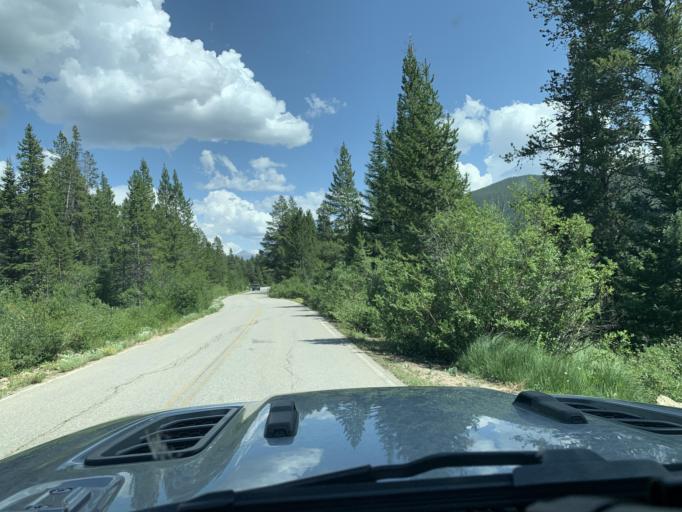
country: US
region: Colorado
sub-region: Lake County
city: Leadville North
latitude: 39.2801
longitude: -106.4377
